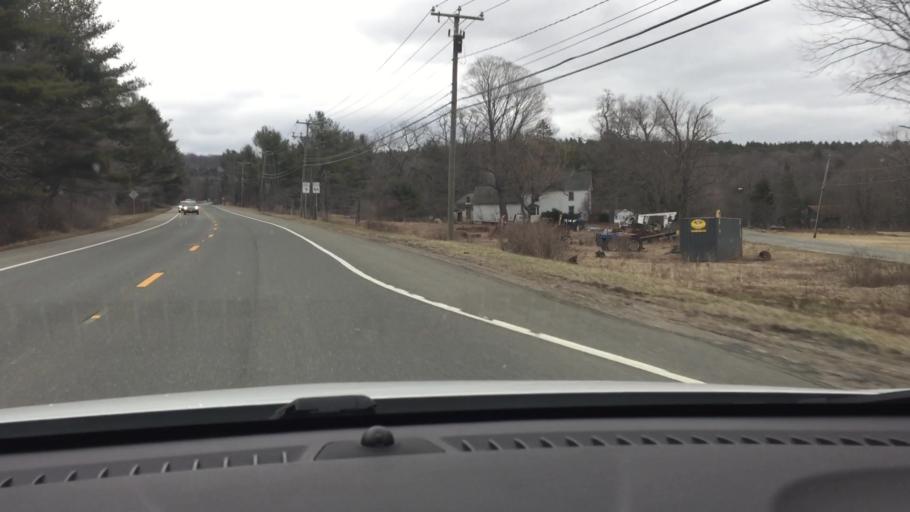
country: US
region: Massachusetts
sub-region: Berkshire County
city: Dalton
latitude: 42.4901
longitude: -73.1238
